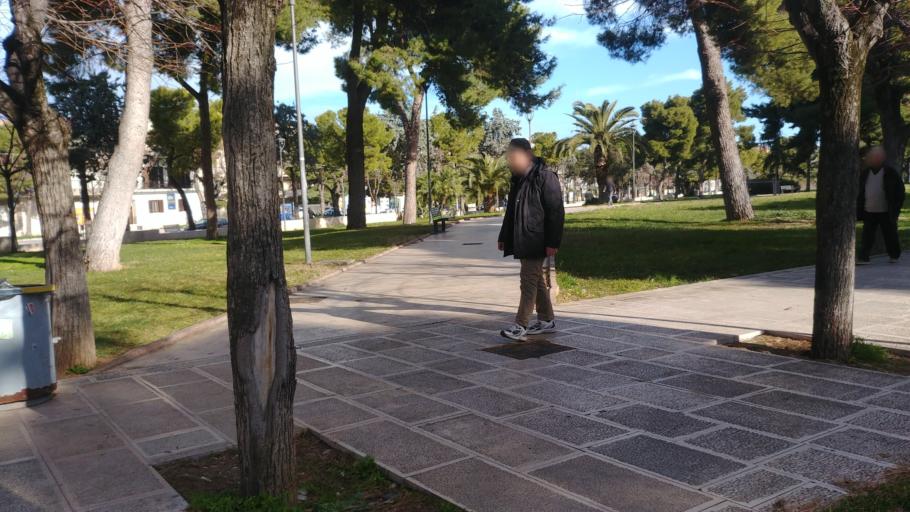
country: IT
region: Apulia
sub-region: Provincia di Barletta - Andria - Trani
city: Andria
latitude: 41.2317
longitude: 16.3056
